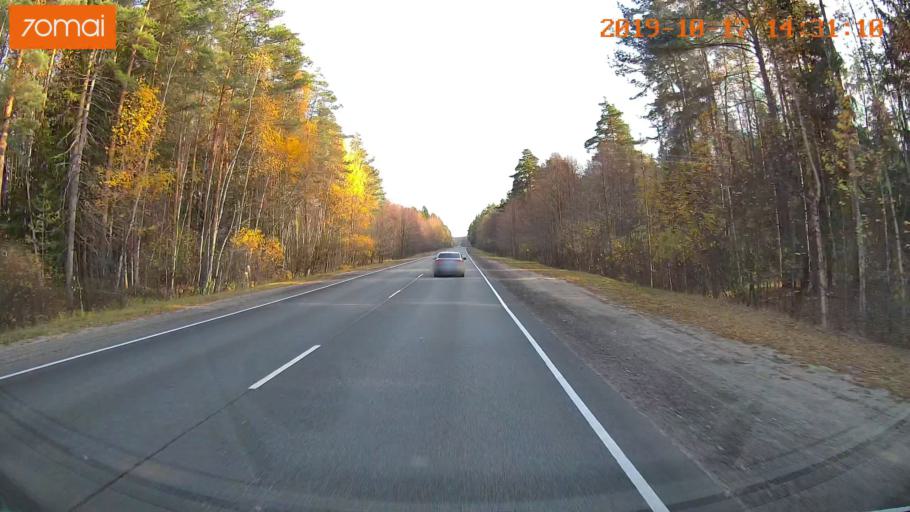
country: RU
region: Rjazan
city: Solotcha
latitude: 54.9391
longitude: 39.9570
